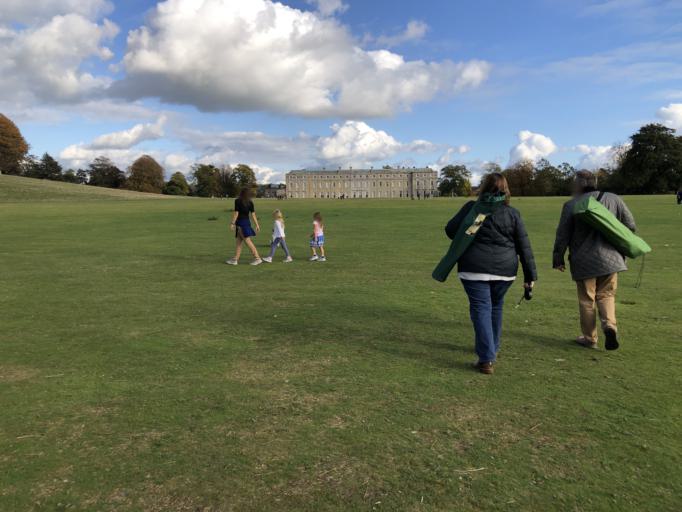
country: GB
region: England
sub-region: West Sussex
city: Petworth
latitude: 50.9883
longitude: -0.6171
